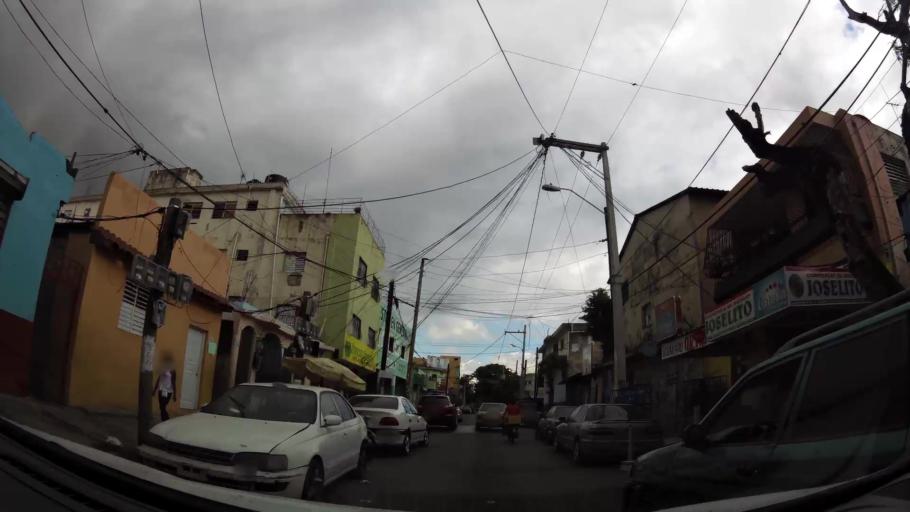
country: DO
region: Nacional
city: San Carlos
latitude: 18.4875
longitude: -69.9084
